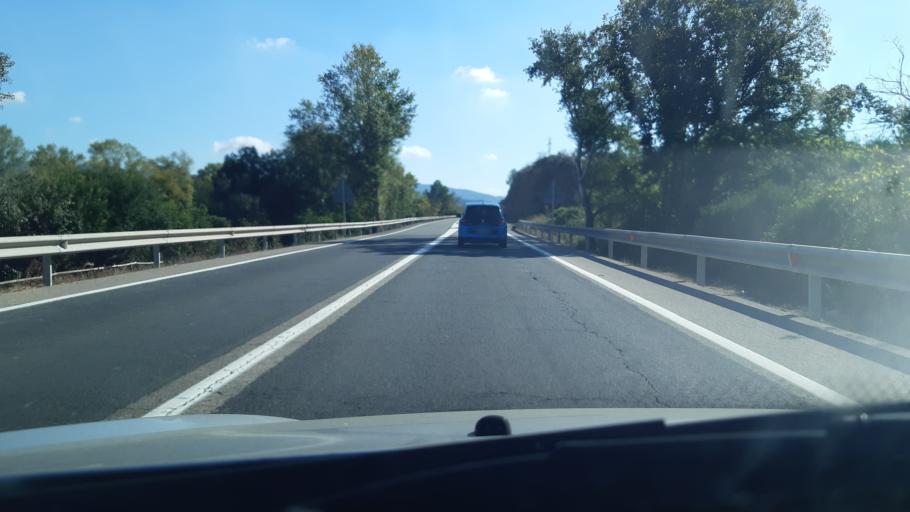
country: ES
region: Catalonia
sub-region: Provincia de Tarragona
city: Tortosa
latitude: 40.8591
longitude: 0.5105
